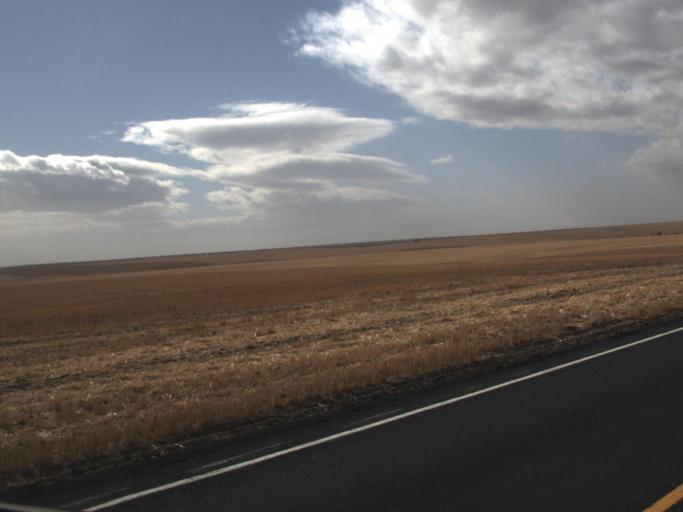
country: US
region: Washington
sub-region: Okanogan County
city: Coulee Dam
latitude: 47.6125
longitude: -118.7628
